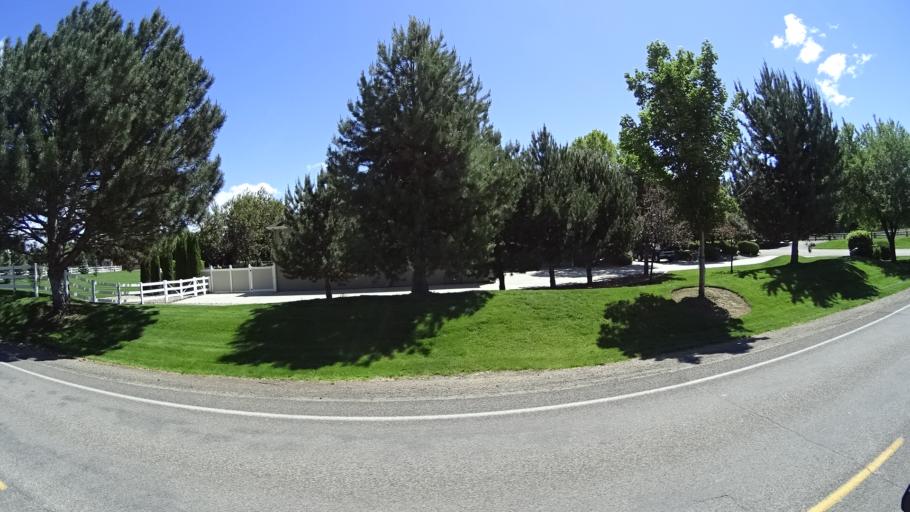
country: US
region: Idaho
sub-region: Ada County
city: Eagle
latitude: 43.6580
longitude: -116.3745
